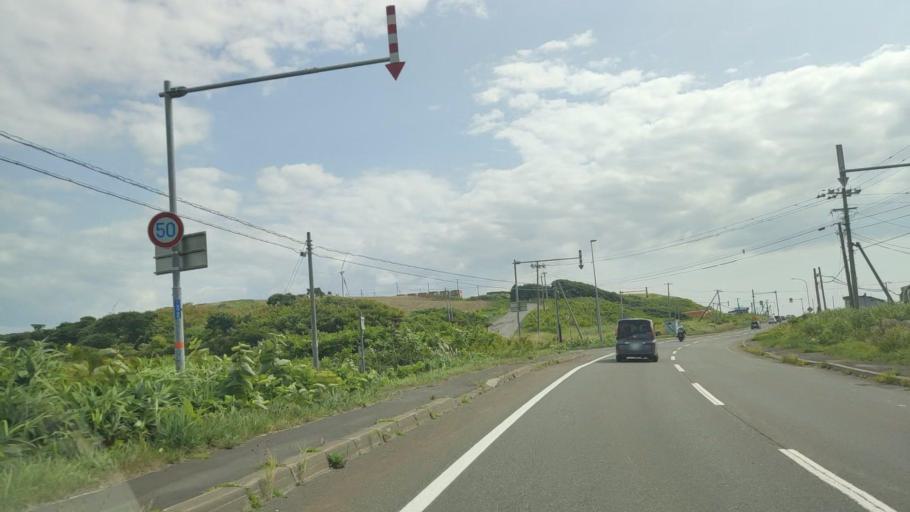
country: JP
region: Hokkaido
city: Rumoi
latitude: 44.2589
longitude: 141.6572
